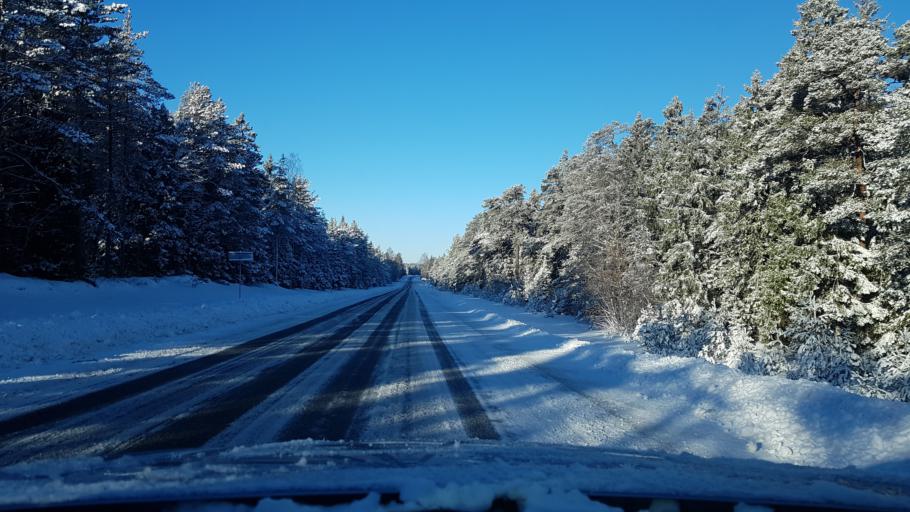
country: EE
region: Hiiumaa
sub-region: Kaerdla linn
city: Kardla
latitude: 58.9603
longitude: 22.8515
